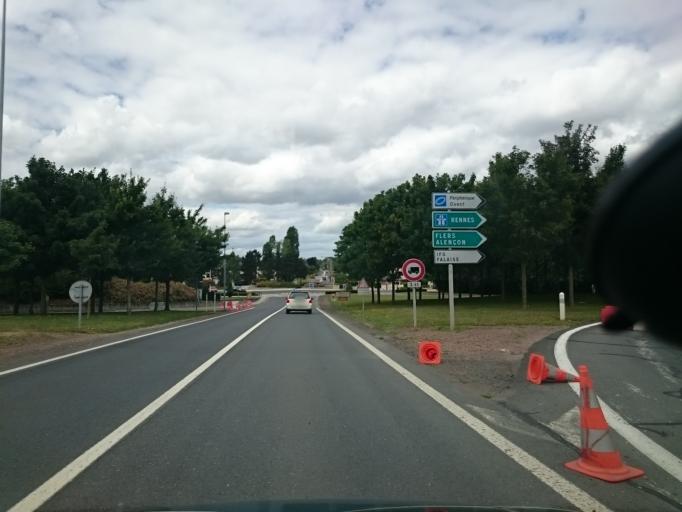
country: FR
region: Lower Normandy
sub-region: Departement du Calvados
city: Cormelles-le-Royal
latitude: 49.1491
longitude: -0.3221
